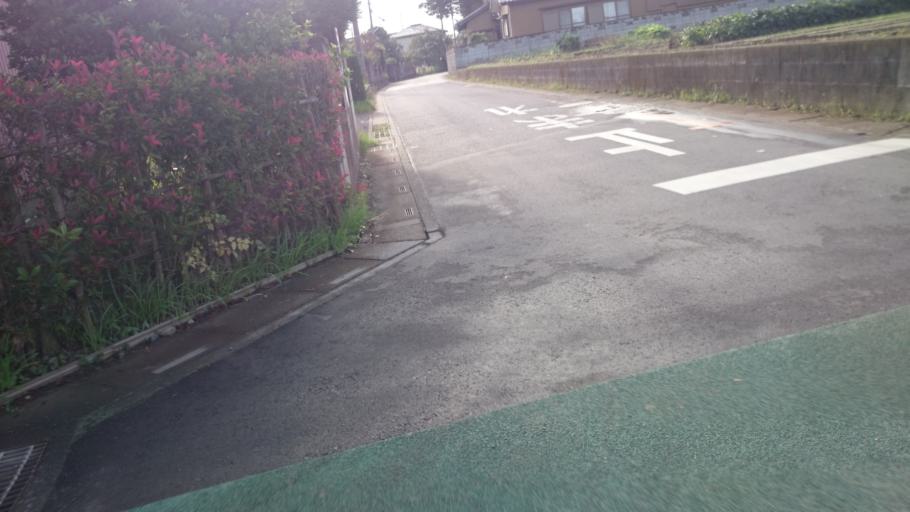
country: JP
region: Saitama
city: Kamifukuoka
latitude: 35.9065
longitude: 139.5679
